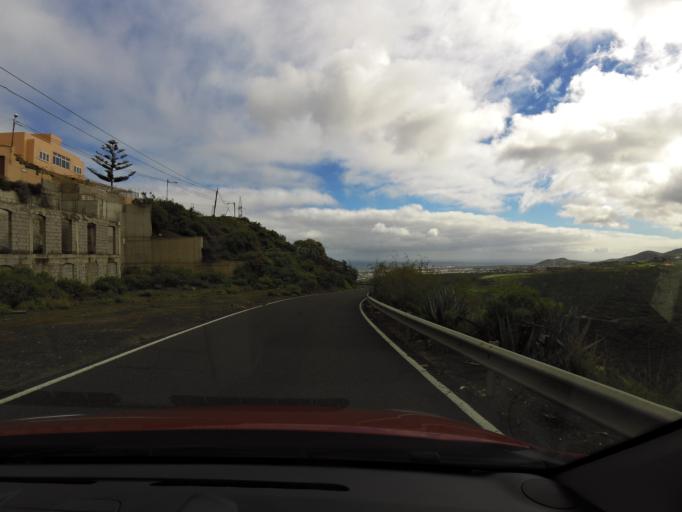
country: ES
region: Canary Islands
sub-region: Provincia de Las Palmas
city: Telde
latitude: 28.0160
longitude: -15.4489
